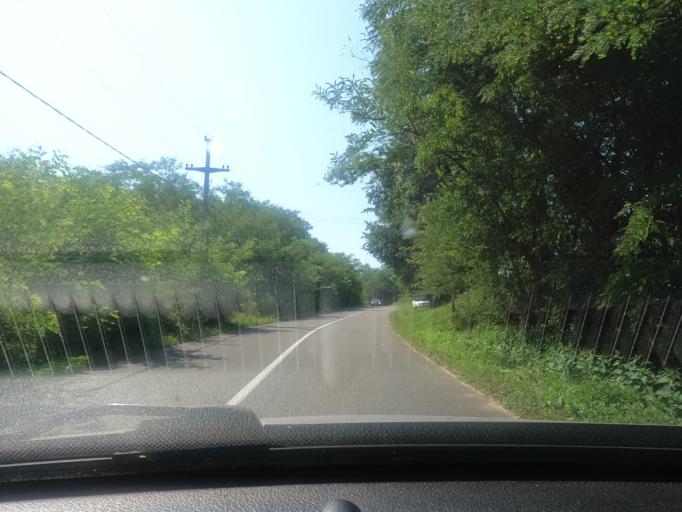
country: RS
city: Kozjak
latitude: 44.5454
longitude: 19.2998
